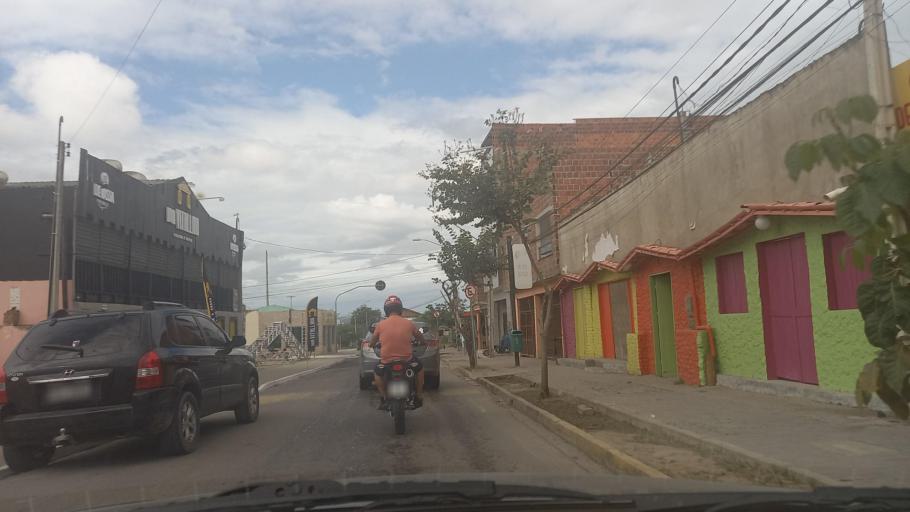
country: BR
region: Pernambuco
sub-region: Caruaru
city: Caruaru
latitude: -8.2903
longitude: -36.0281
